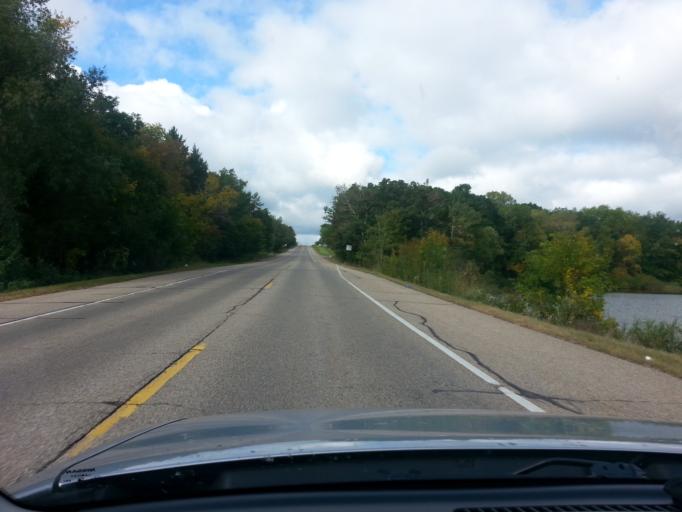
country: US
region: Minnesota
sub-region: Washington County
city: Lake Elmo
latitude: 44.9635
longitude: -92.9115
